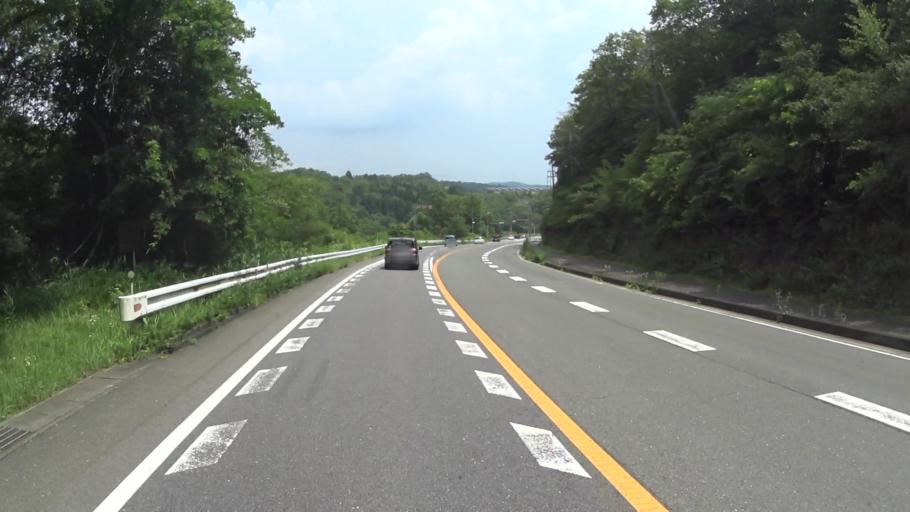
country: JP
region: Mie
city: Ueno-ebisumachi
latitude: 34.7704
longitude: 136.0214
